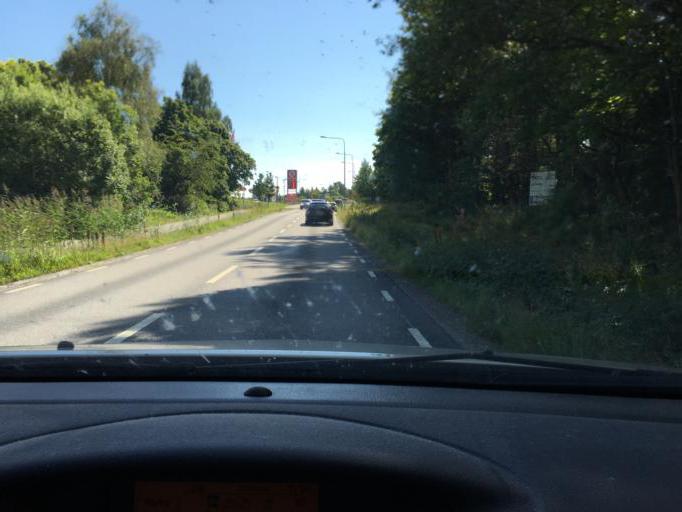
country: SE
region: Stockholm
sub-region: Varmdo Kommun
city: Mortnas
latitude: 59.2836
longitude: 18.4239
